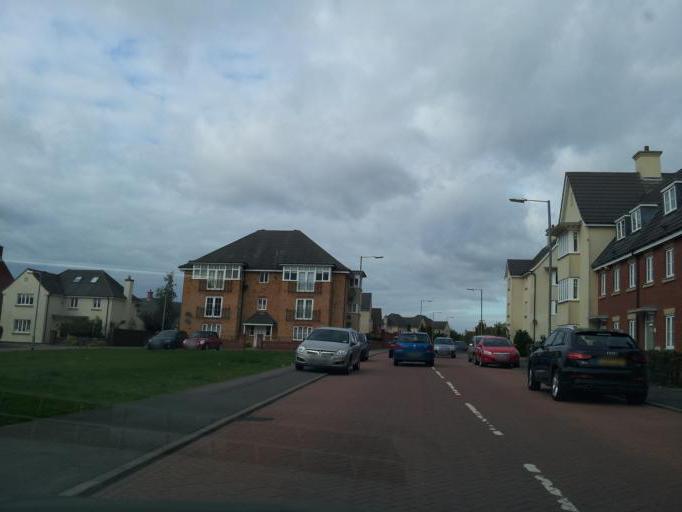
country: GB
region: England
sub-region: Northamptonshire
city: Bugbrooke
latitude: 52.2475
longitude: -0.9631
